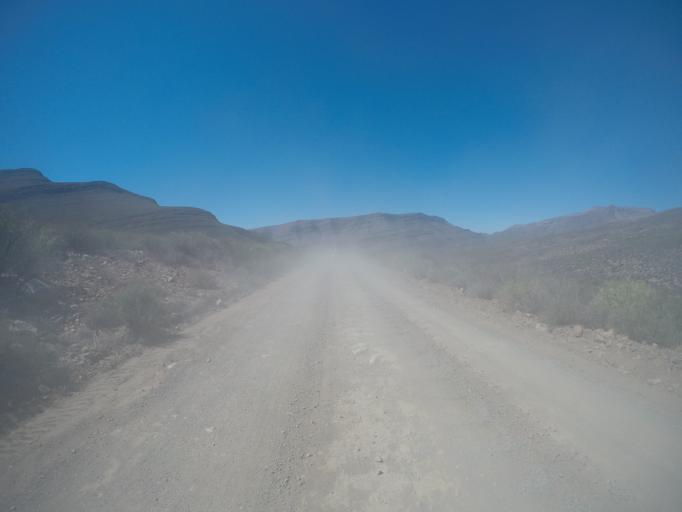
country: ZA
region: Western Cape
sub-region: West Coast District Municipality
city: Clanwilliam
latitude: -32.6212
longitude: 19.3851
